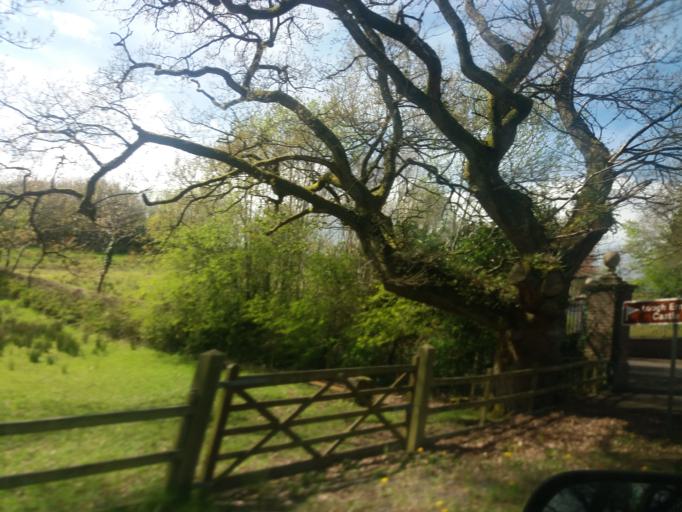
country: GB
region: Northern Ireland
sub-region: Fermanagh District
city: Enniskillen
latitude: 54.3921
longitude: -7.7014
